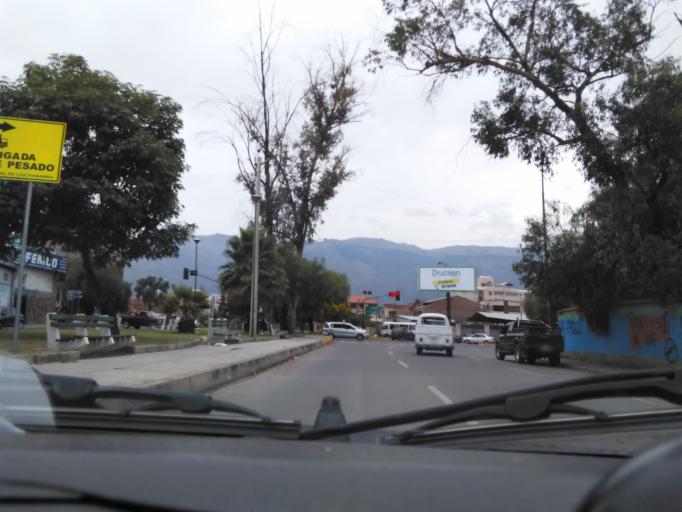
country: BO
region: Cochabamba
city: Cochabamba
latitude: -17.3880
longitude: -66.1824
